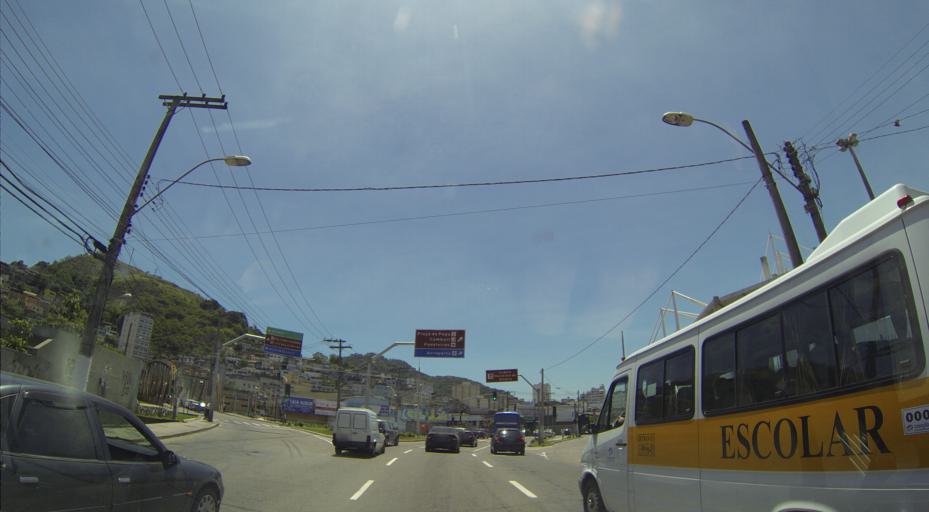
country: BR
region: Espirito Santo
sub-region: Vitoria
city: Vitoria
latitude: -20.3211
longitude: -40.3489
